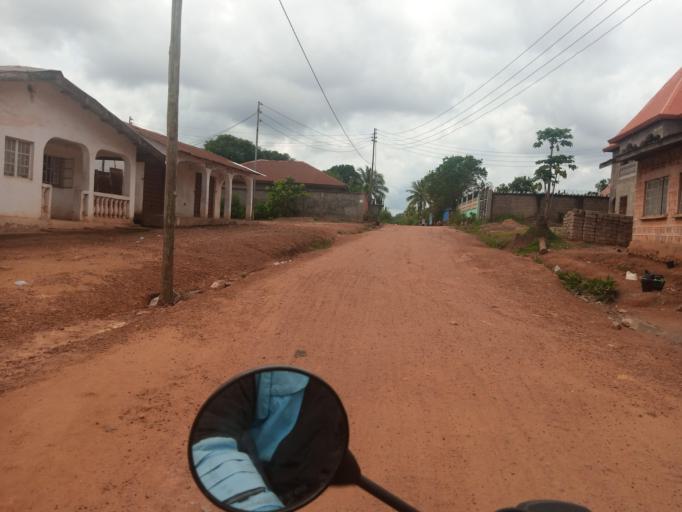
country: SL
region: Southern Province
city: Bo
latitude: 7.9513
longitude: -11.7546
